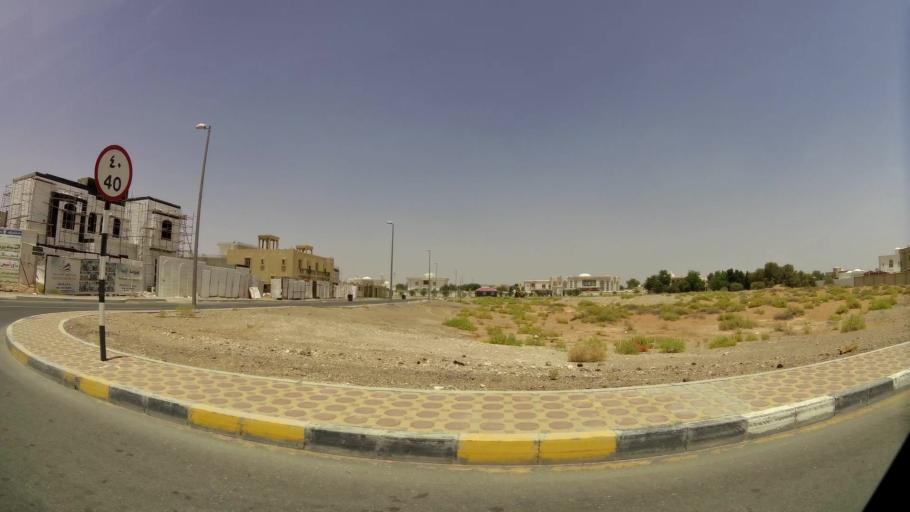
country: OM
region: Al Buraimi
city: Al Buraymi
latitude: 24.2680
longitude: 55.7097
